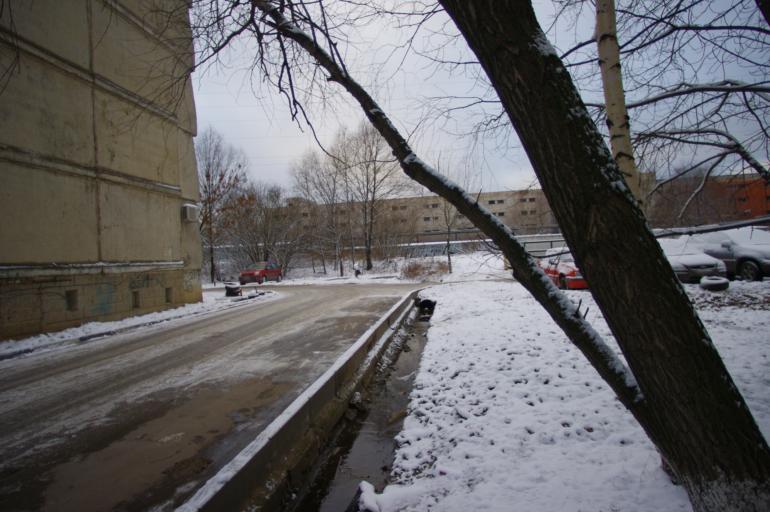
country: RU
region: Moskovskaya
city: Krasnogorsk
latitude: 55.8086
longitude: 37.3224
